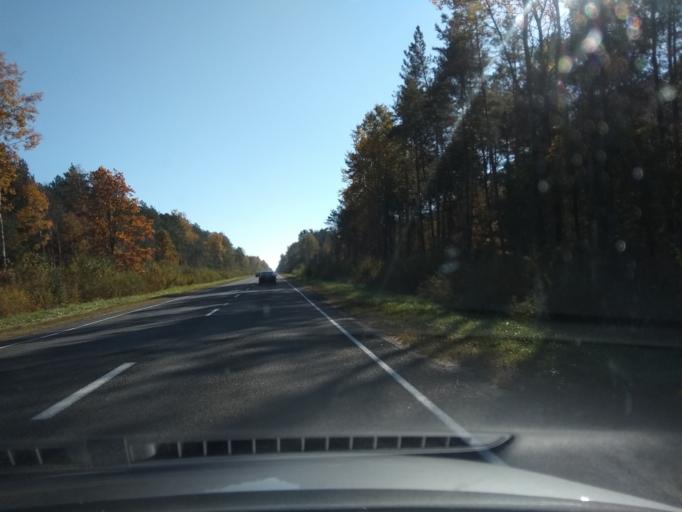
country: BY
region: Brest
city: Malaryta
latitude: 51.9004
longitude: 24.1232
